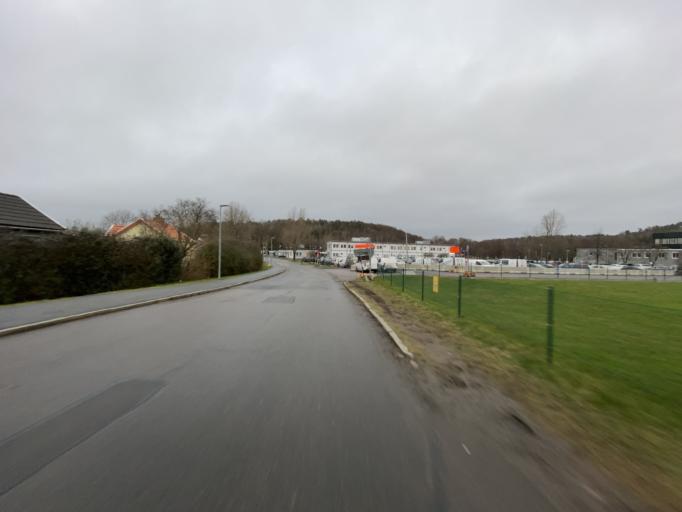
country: SE
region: Vaestra Goetaland
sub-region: Goteborg
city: Eriksbo
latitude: 57.7211
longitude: 12.0472
